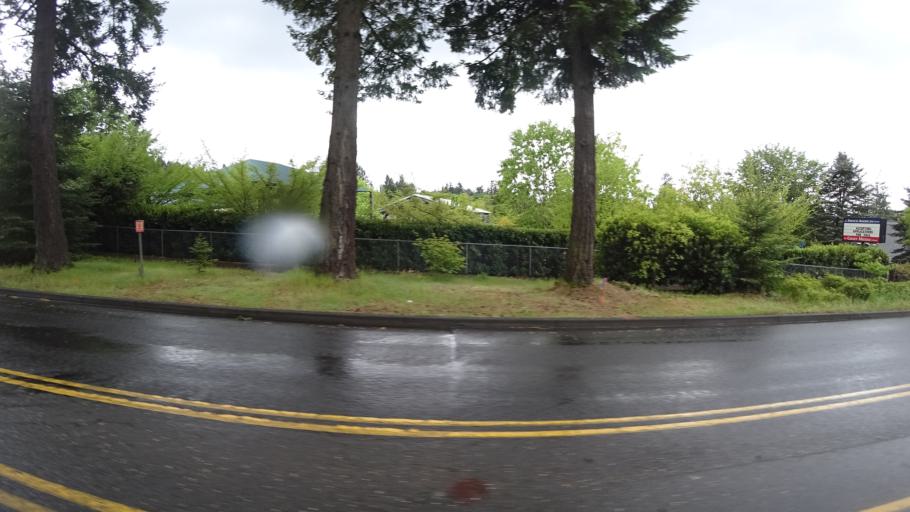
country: US
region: Oregon
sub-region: Washington County
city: West Haven
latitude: 45.5296
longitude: -122.7649
